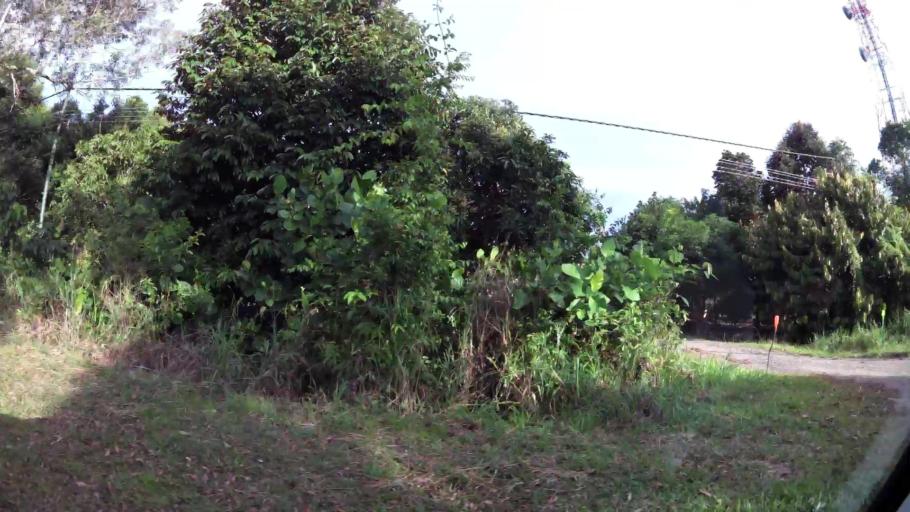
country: BN
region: Brunei and Muara
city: Bandar Seri Begawan
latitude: 4.9588
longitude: 115.0224
